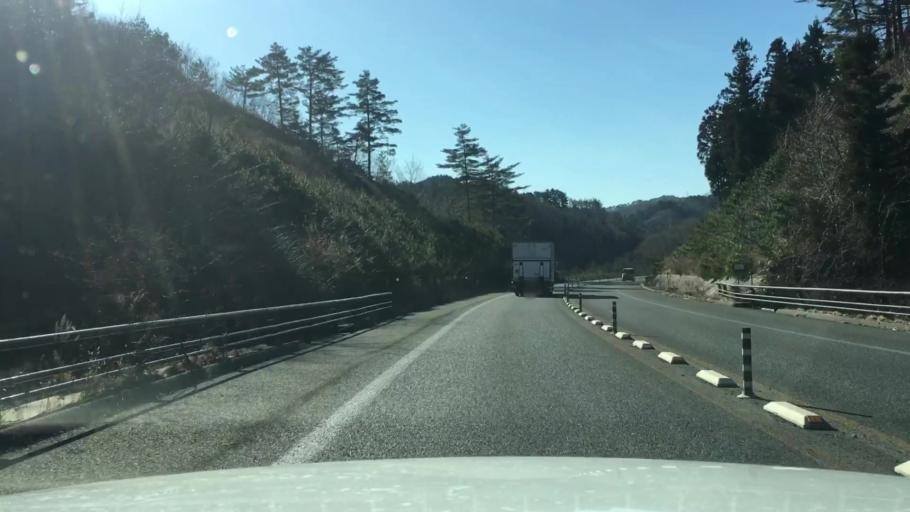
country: JP
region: Iwate
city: Miyako
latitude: 39.6128
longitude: 141.9349
